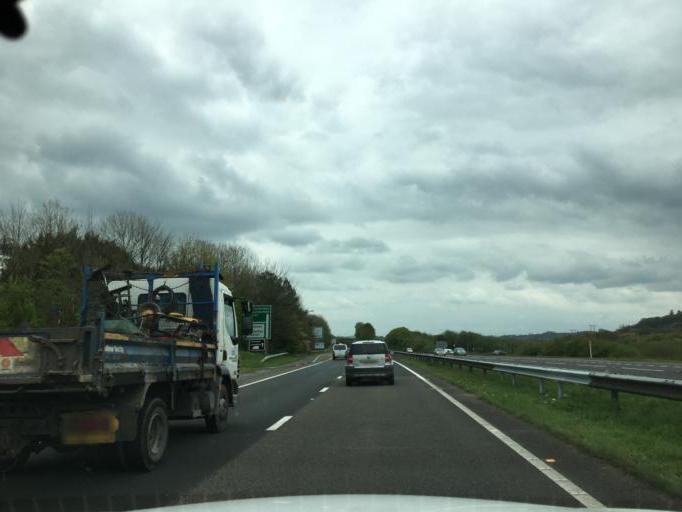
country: GB
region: Wales
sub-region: Carmarthenshire
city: Llangain
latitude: 51.8479
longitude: -4.3478
